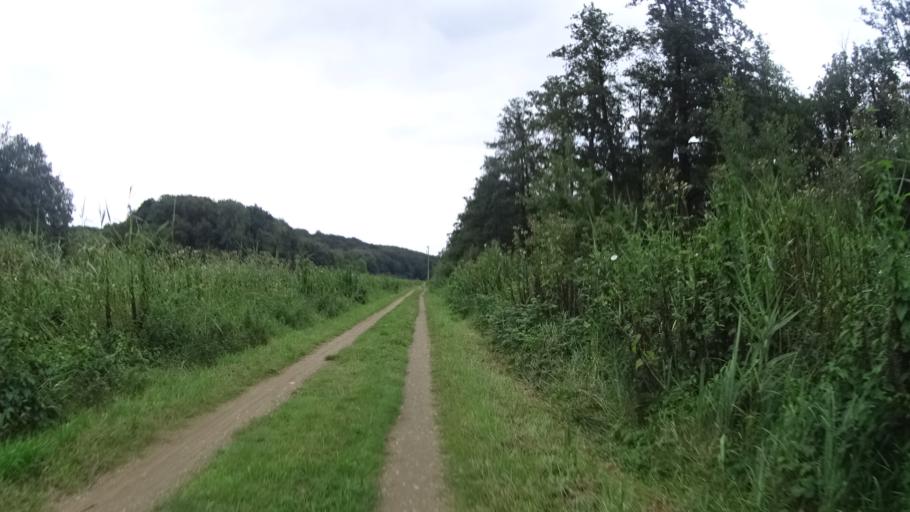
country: DE
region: Schleswig-Holstein
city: Alt Molln
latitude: 53.6397
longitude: 10.6587
